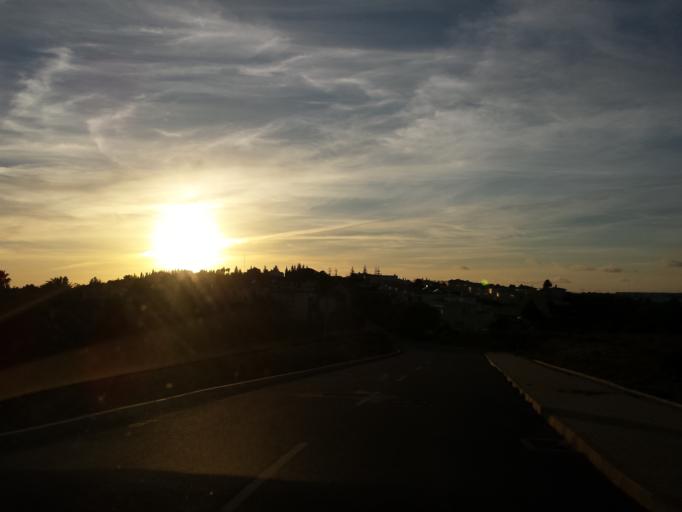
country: PT
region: Faro
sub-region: Lagos
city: Lagos
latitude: 37.1246
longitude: -8.6542
